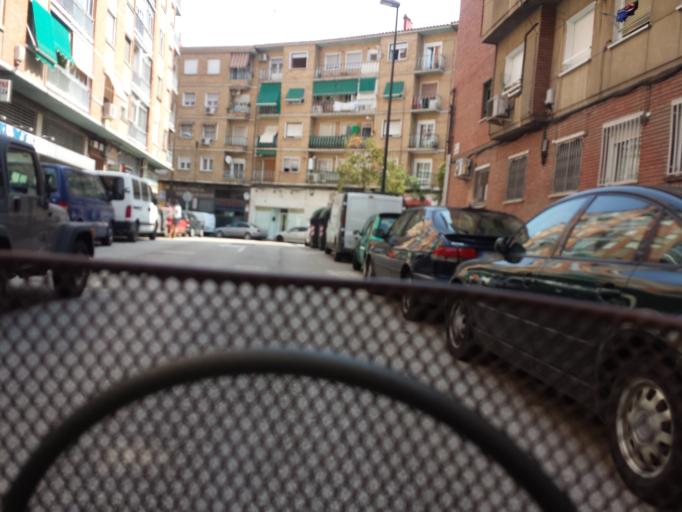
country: ES
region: Aragon
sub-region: Provincia de Zaragoza
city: Delicias
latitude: 41.6509
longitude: -0.9119
